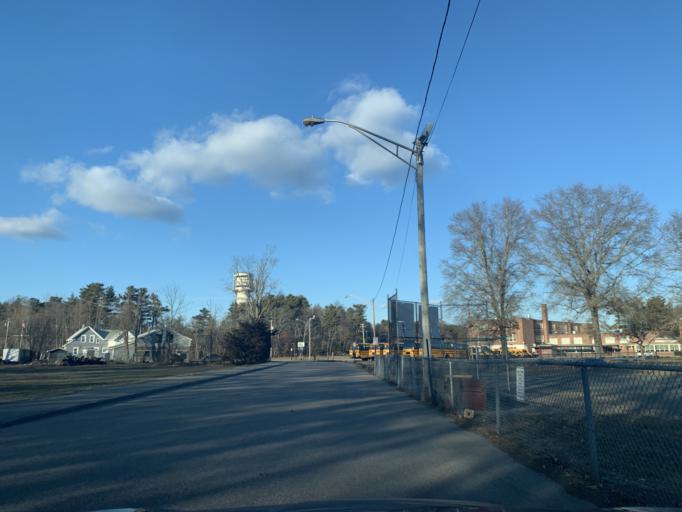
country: US
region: Massachusetts
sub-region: Bristol County
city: Norton
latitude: 41.9614
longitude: -71.1938
